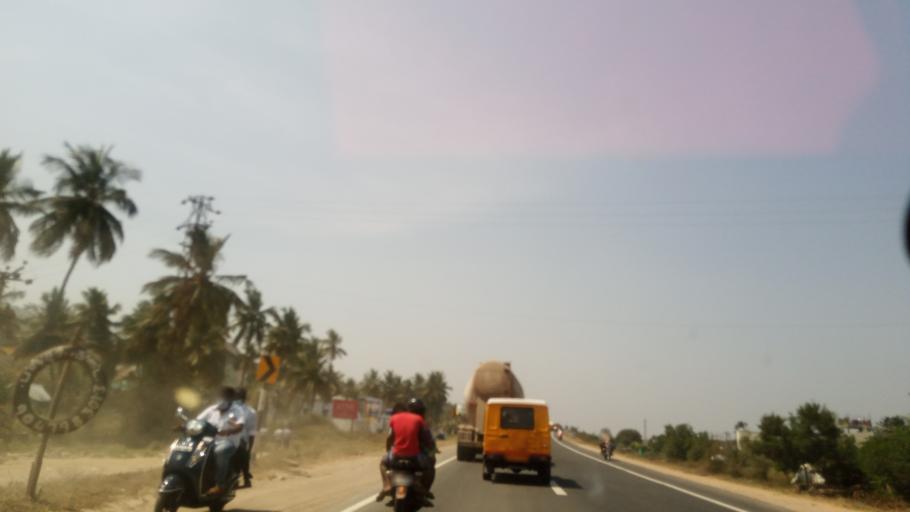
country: IN
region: Tamil Nadu
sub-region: Salem
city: Salem
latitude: 11.6602
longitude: 78.2179
